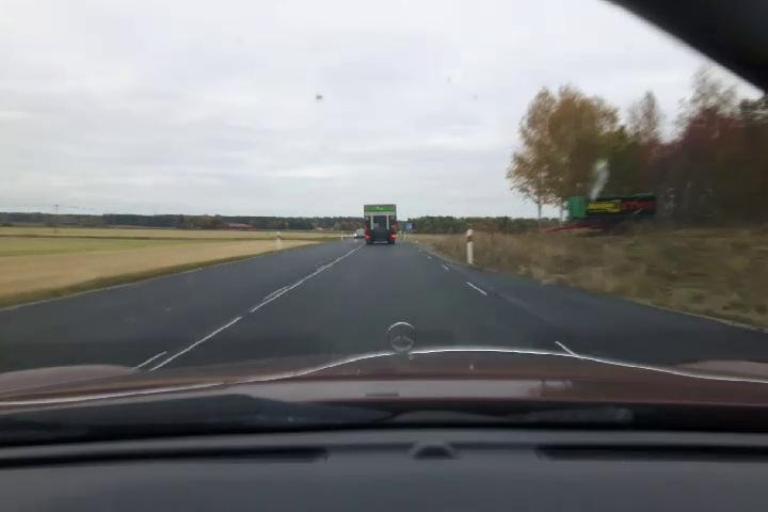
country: SE
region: Uppsala
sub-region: Enkopings Kommun
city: Enkoping
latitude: 59.6288
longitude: 17.0477
